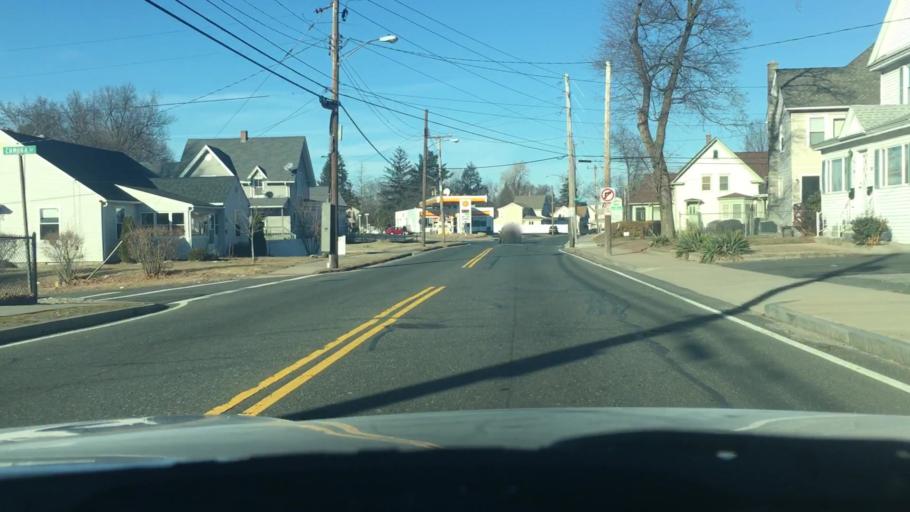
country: US
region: Massachusetts
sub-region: Hampden County
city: Ludlow
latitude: 42.1623
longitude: -72.4838
